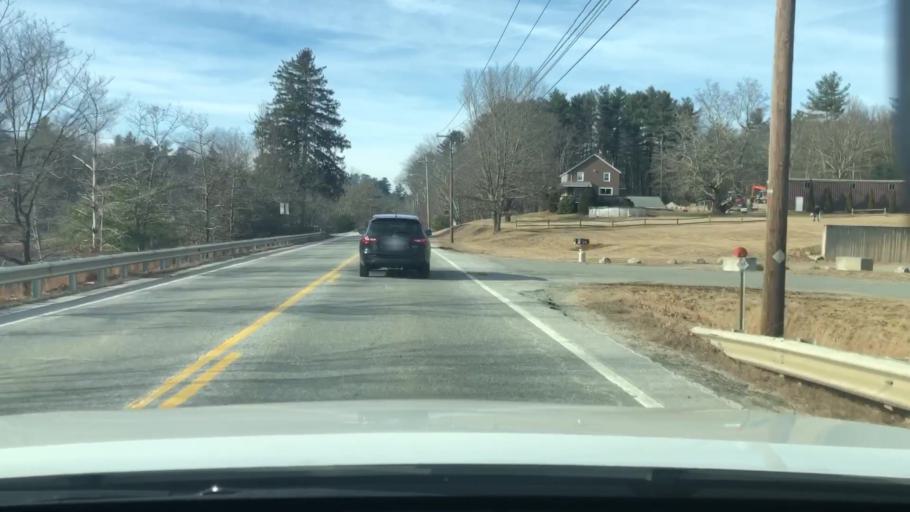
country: US
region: Massachusetts
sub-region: Worcester County
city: Northbridge
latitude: 42.1803
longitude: -71.6412
